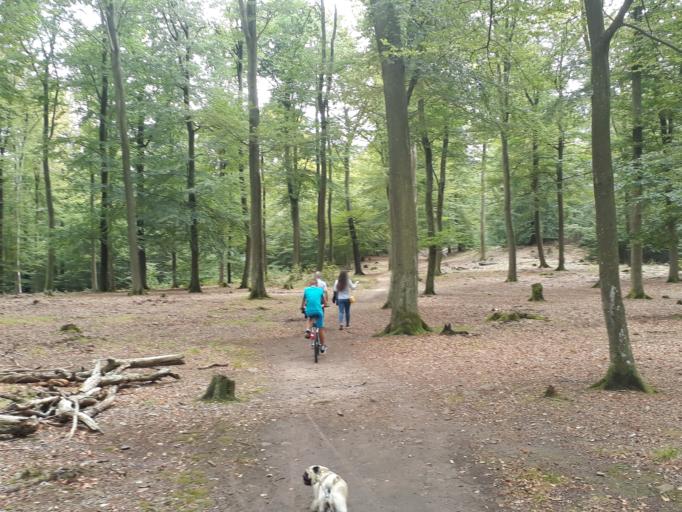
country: DE
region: Rheinland-Pfalz
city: Kaiserslautern
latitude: 49.4274
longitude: 7.7880
